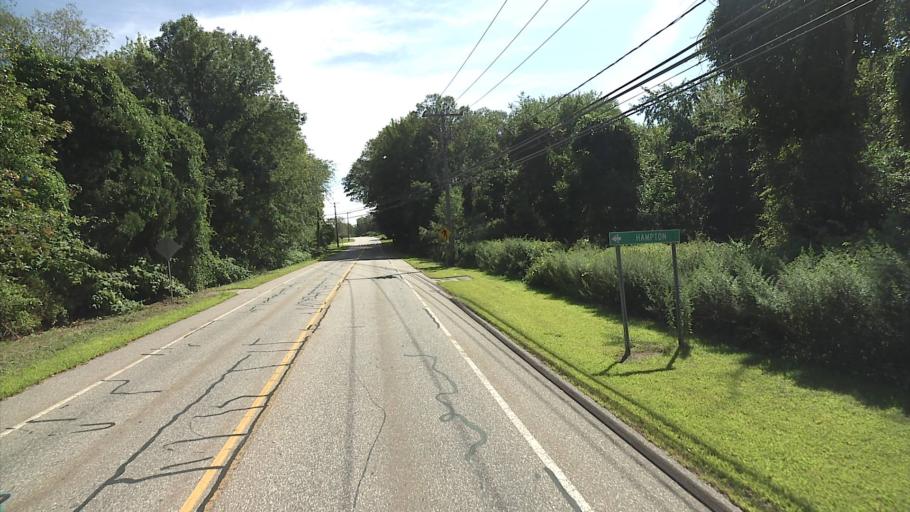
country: US
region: Connecticut
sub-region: New London County
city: Baltic
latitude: 41.6987
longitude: -72.0712
